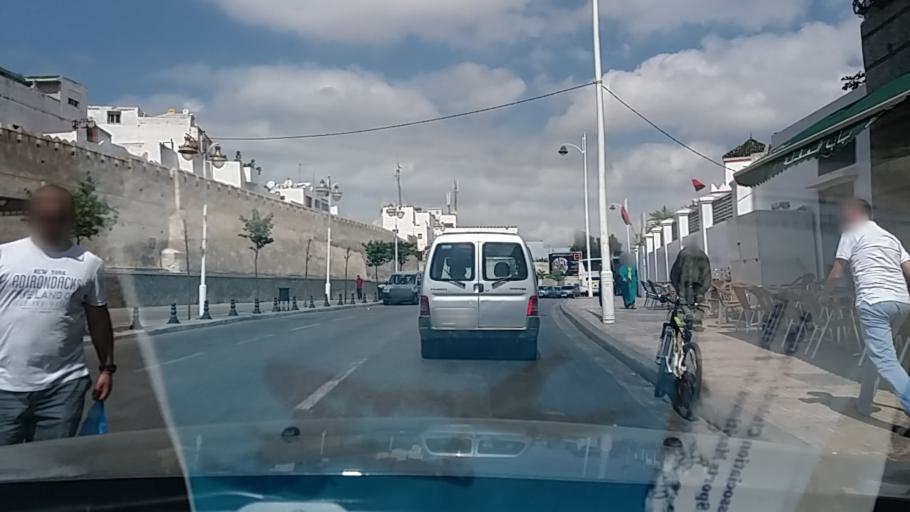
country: MA
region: Tanger-Tetouan
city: Tetouan
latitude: 35.5708
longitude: -5.3635
